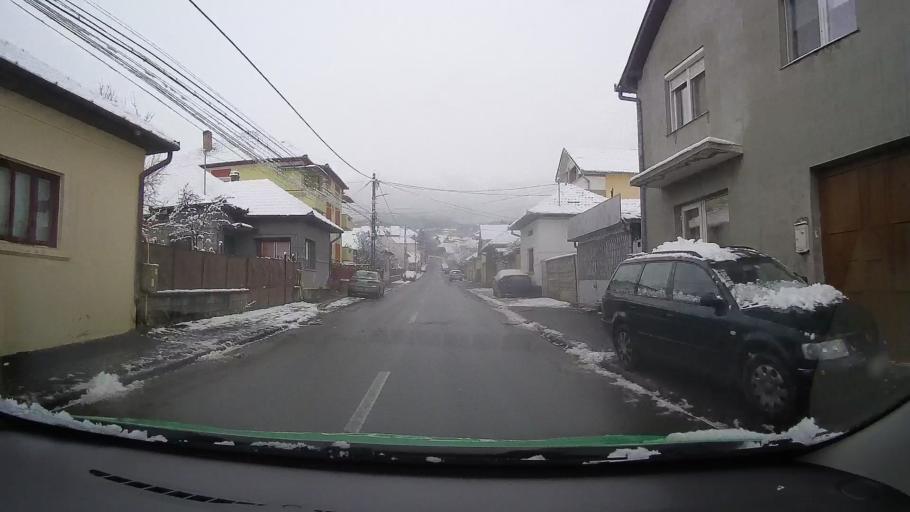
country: RO
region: Hunedoara
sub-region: Municipiul Deva
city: Deva
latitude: 45.8719
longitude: 22.9001
